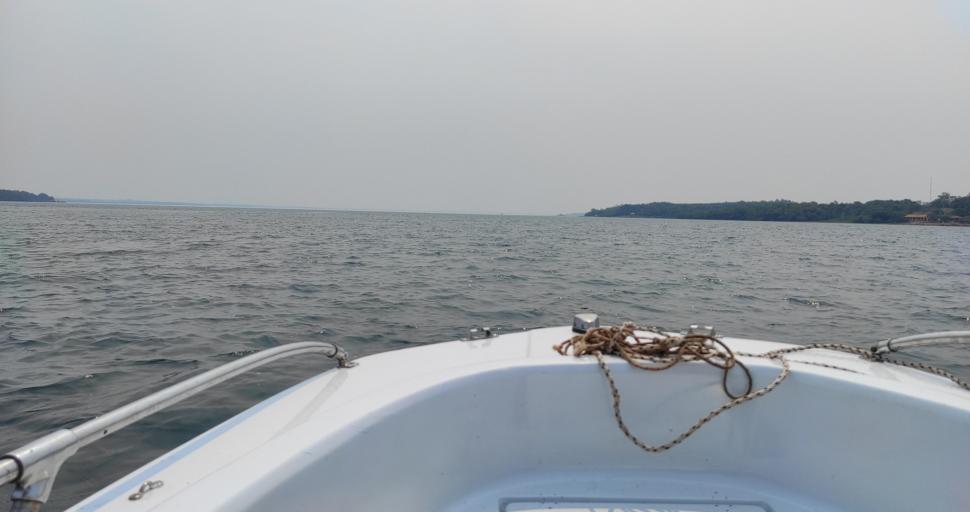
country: AR
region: Misiones
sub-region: Departamento de Candelaria
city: Candelaria
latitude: -27.4463
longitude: -55.7499
